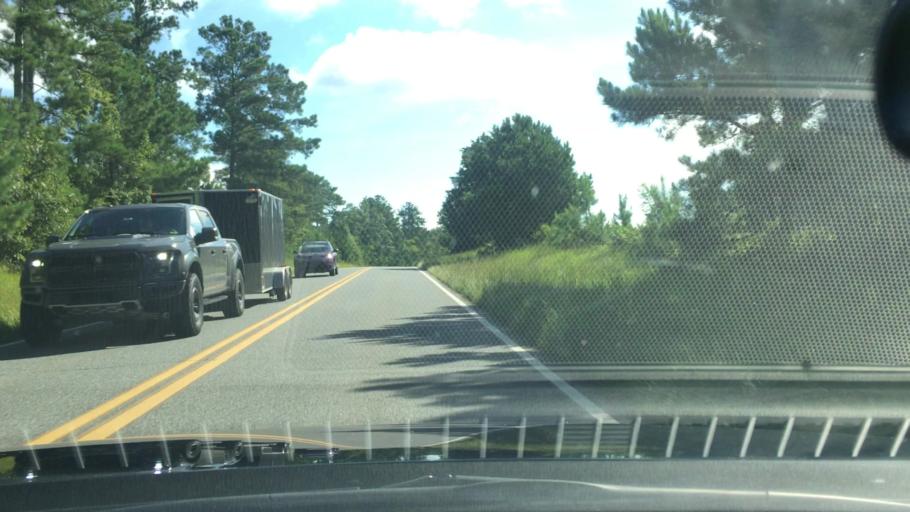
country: US
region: Georgia
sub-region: Putnam County
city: Jefferson
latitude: 33.4516
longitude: -83.3056
